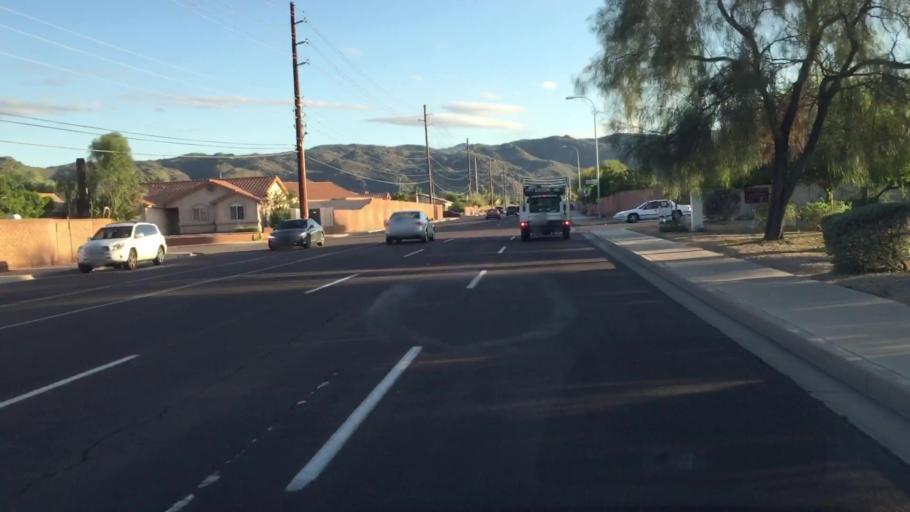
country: US
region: Arizona
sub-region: Maricopa County
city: Phoenix
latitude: 33.3855
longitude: -112.0474
